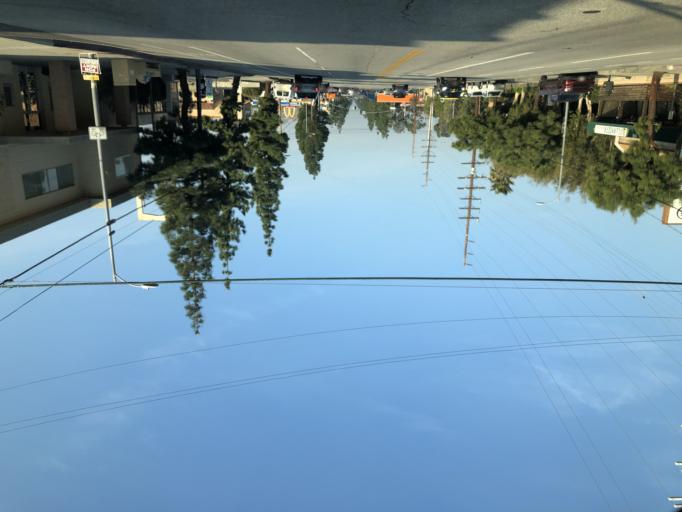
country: US
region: California
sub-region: Los Angeles County
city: Chatsworth
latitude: 34.2572
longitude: -118.5910
